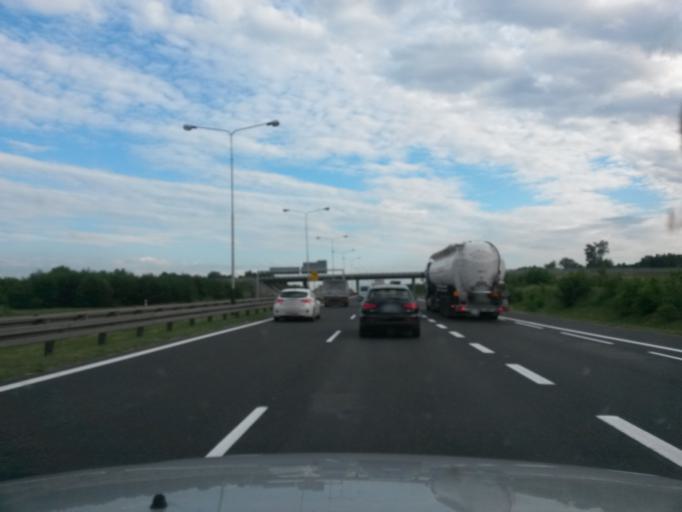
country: PL
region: Lodz Voivodeship
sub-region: Piotrkow Trybunalski
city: Piotrkow Trybunalski
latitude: 51.4284
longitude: 19.6404
